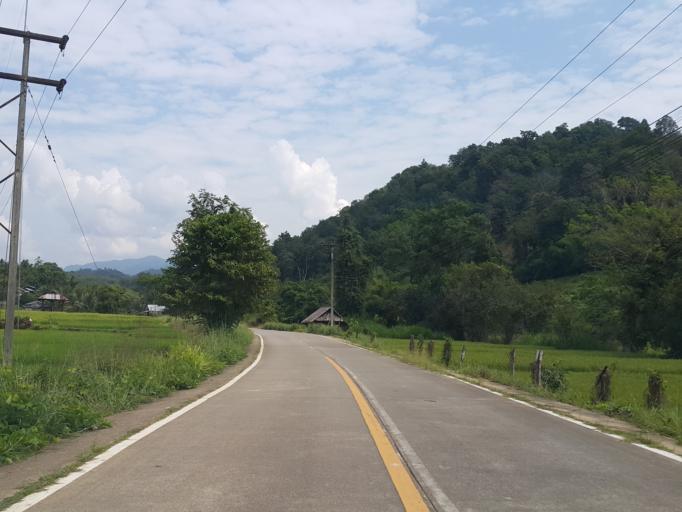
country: TH
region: Mae Hong Son
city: Mae Hong Son
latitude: 19.4603
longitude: 97.9669
